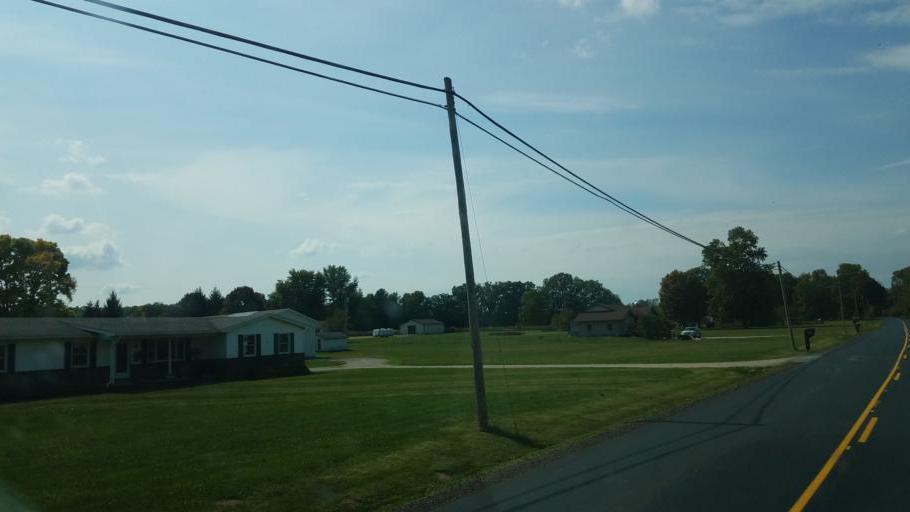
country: US
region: Ohio
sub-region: Knox County
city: Mount Vernon
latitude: 40.3999
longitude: -82.5405
